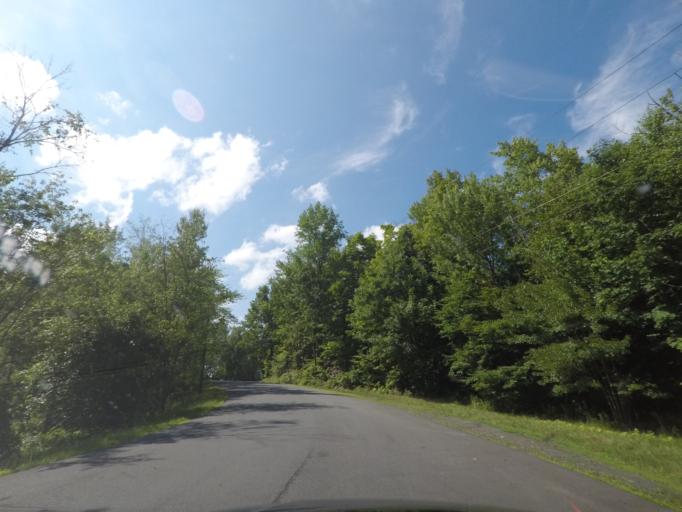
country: US
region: New York
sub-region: Rensselaer County
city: Averill Park
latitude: 42.6055
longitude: -73.5831
